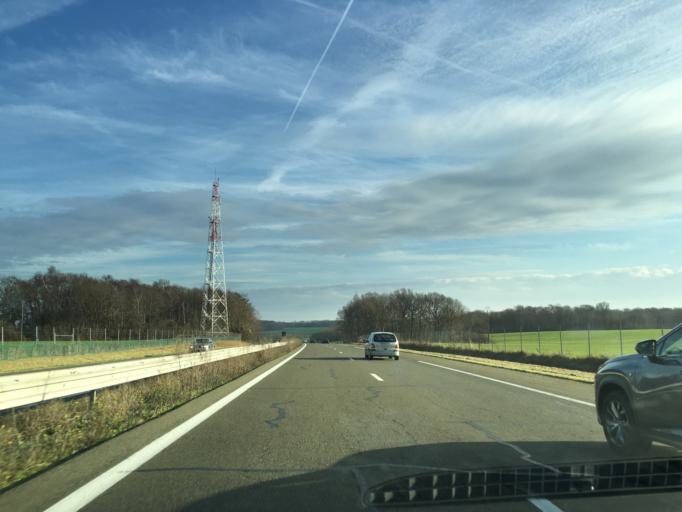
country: FR
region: Picardie
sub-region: Departement de l'Aisne
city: Montreuil-aux-Lions
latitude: 49.0395
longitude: 3.2325
